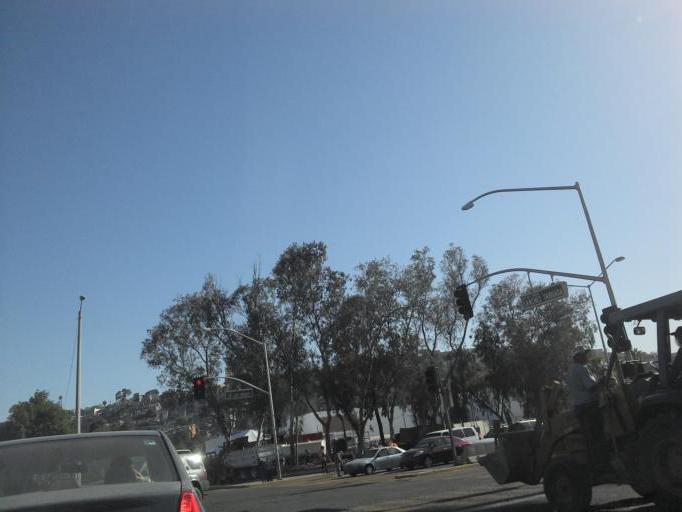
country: MX
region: Baja California
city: Tijuana
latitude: 32.5177
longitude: -117.0050
